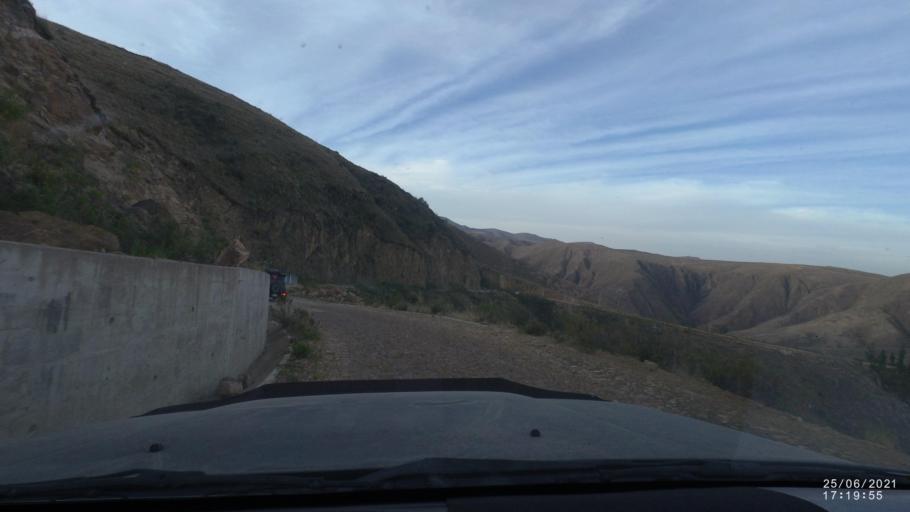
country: BO
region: Cochabamba
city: Arani
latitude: -17.9036
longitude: -65.6917
